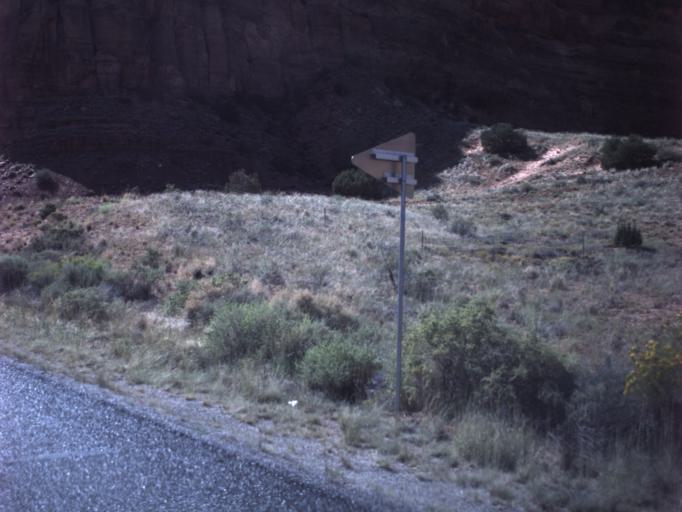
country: US
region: Utah
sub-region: Grand County
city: Moab
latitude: 38.6565
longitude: -109.7147
